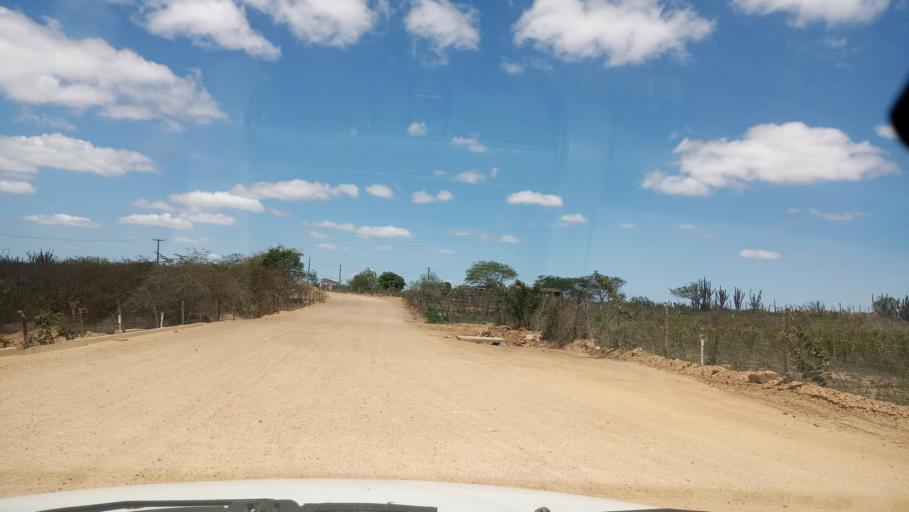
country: BR
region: Rio Grande do Norte
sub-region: Sao Paulo Do Potengi
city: Sao Paulo do Potengi
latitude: -5.7870
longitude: -35.9157
